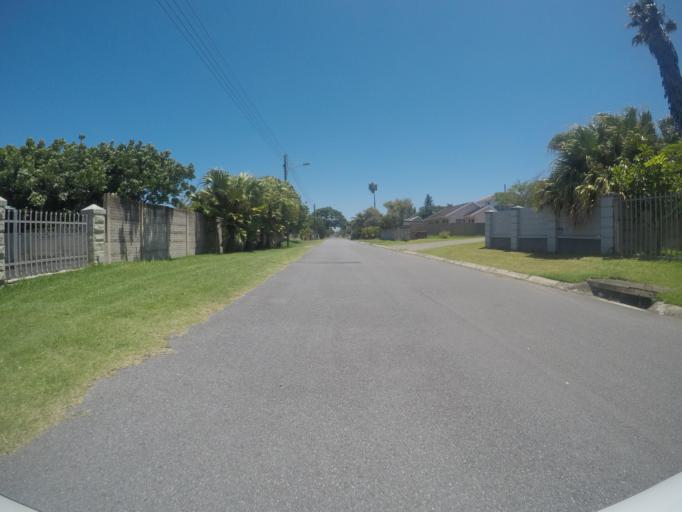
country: ZA
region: Eastern Cape
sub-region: Buffalo City Metropolitan Municipality
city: East London
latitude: -32.9496
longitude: 28.0136
